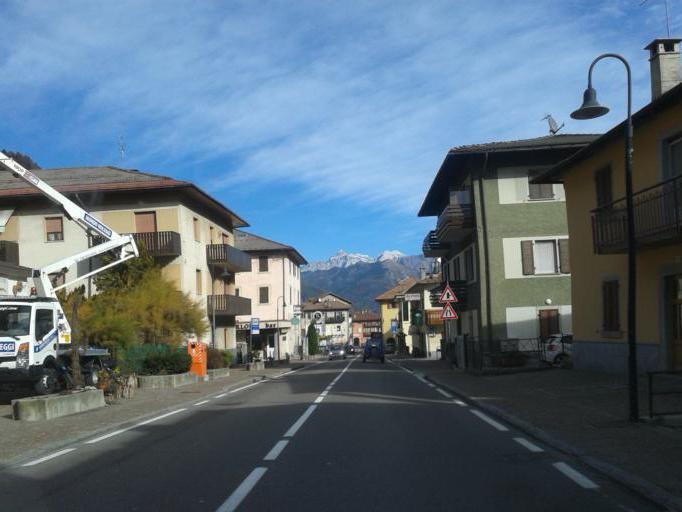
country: IT
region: Trentino-Alto Adige
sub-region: Provincia di Trento
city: Breguzzo
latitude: 46.0059
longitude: 10.6974
